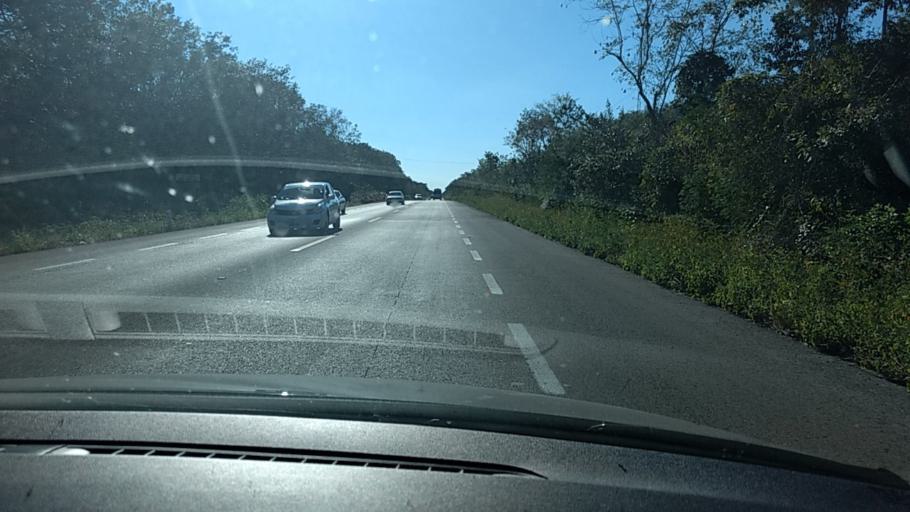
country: MX
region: Yucatan
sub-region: Uayma
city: Uayma
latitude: 20.6339
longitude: -88.3457
